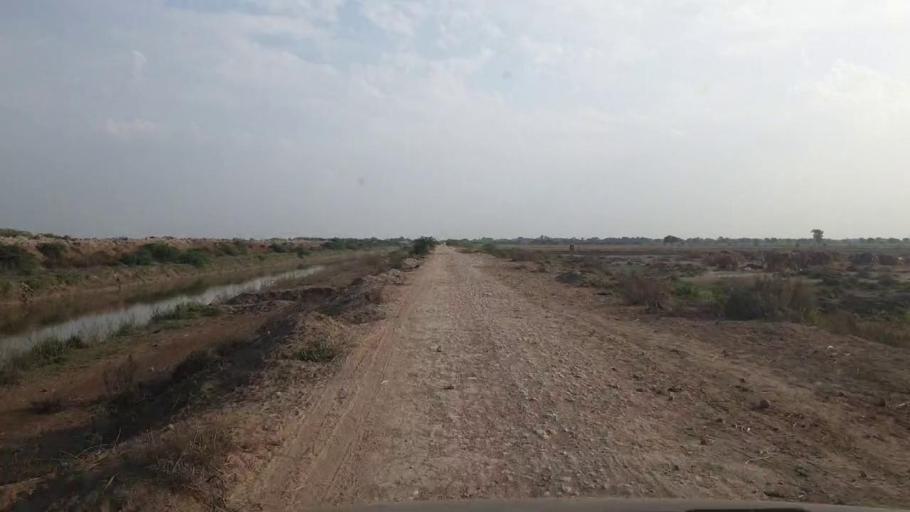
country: PK
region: Sindh
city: Badin
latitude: 24.5584
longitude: 68.6691
